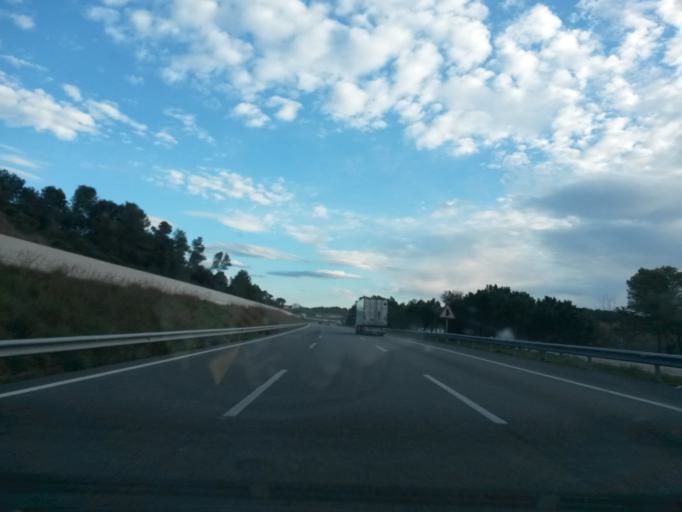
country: ES
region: Catalonia
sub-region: Provincia de Girona
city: Cervia de Ter
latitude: 42.0798
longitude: 2.8899
